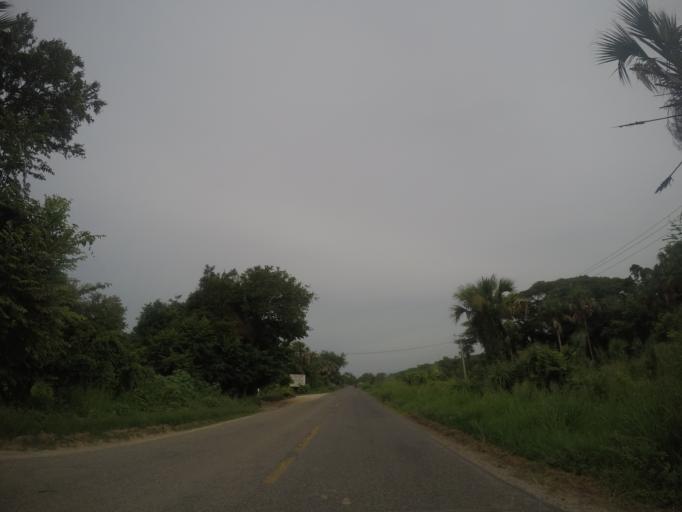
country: MX
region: Oaxaca
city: San Pedro Mixtepec
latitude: 15.9273
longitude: -97.1491
